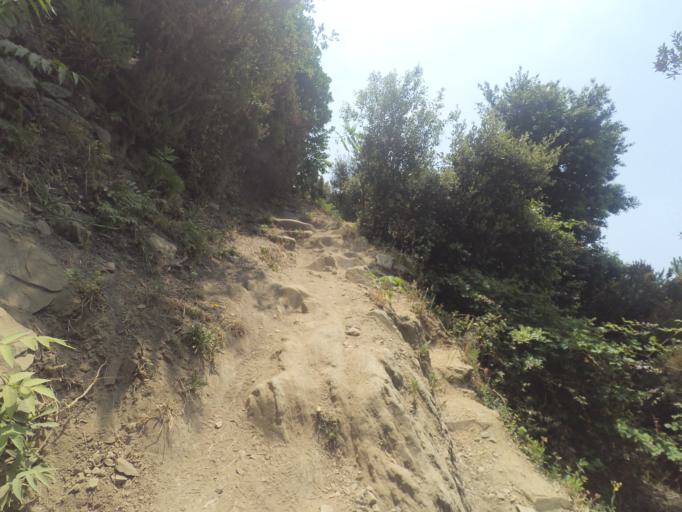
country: IT
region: Liguria
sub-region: Provincia di La Spezia
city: Vernazza
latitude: 44.1244
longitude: 9.7155
